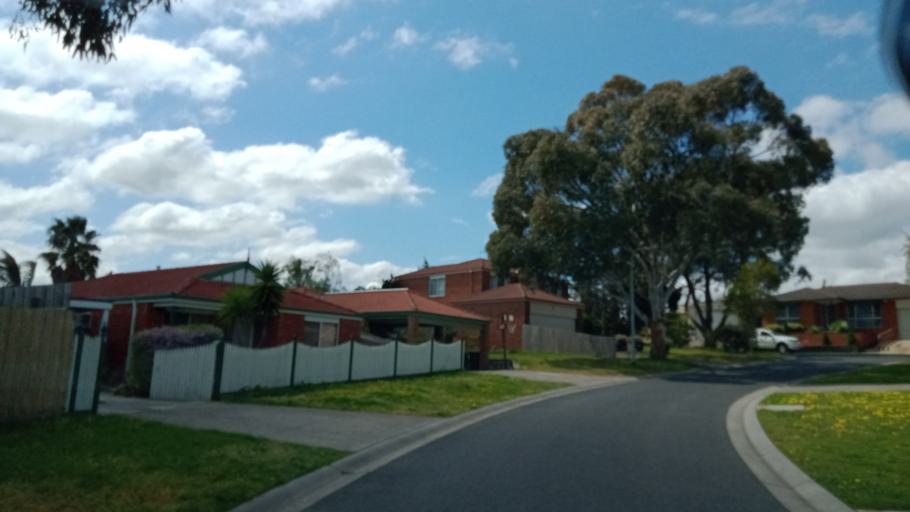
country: AU
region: Victoria
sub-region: Frankston
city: Sandhurst
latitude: -38.0908
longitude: 145.2019
